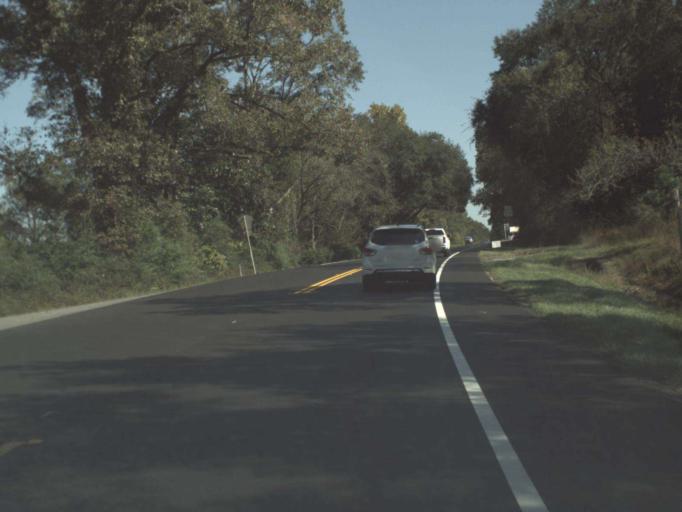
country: US
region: Florida
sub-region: Walton County
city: DeFuniak Springs
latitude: 30.8220
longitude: -86.2164
